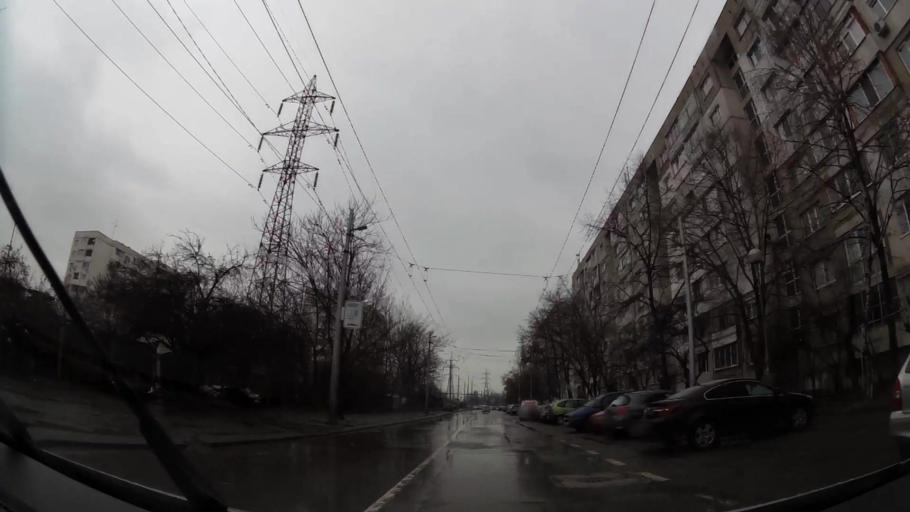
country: BG
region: Sofia-Capital
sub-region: Stolichna Obshtina
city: Sofia
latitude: 42.6698
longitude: 23.3861
